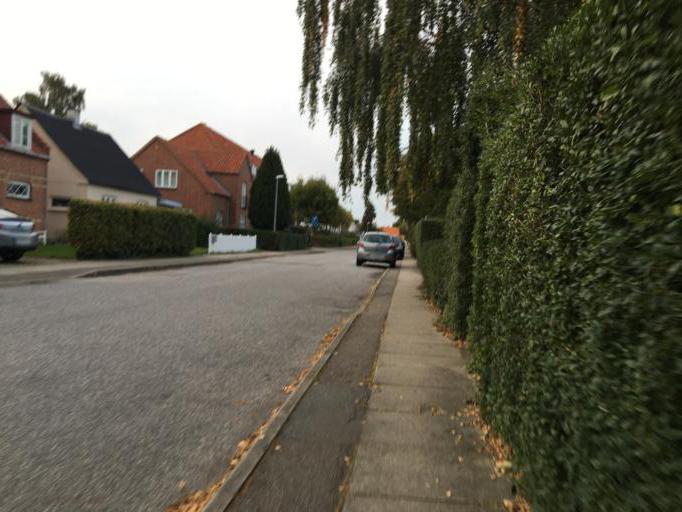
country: DK
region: Capital Region
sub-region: Tarnby Kommune
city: Tarnby
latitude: 55.6369
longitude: 12.6273
